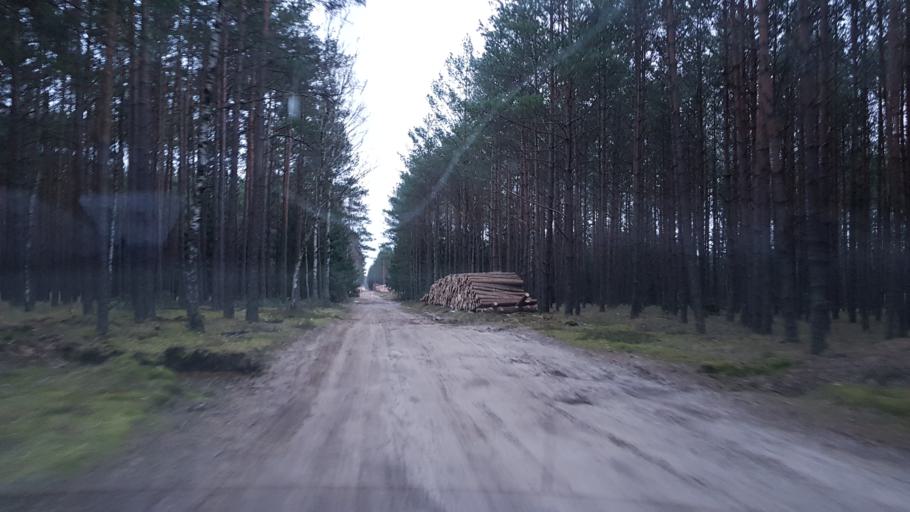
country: PL
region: Greater Poland Voivodeship
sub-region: Powiat zlotowski
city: Sypniewo
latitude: 53.5007
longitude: 16.6767
